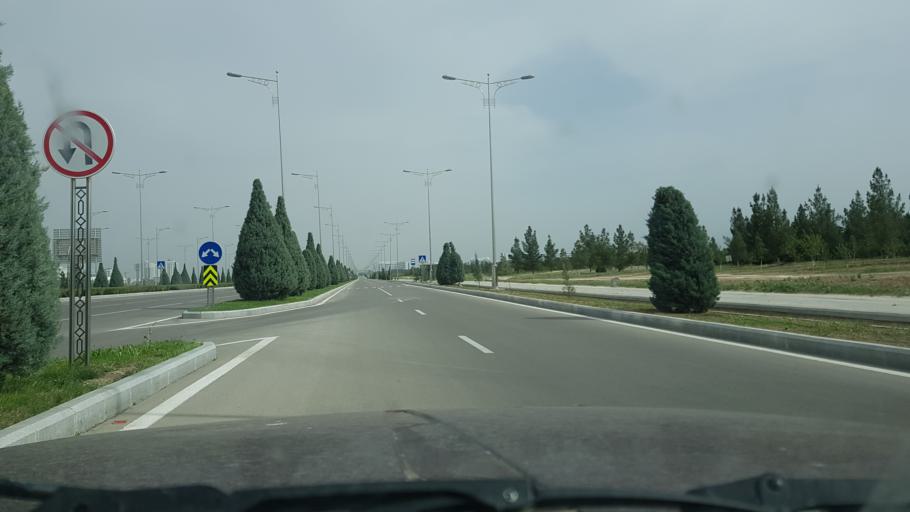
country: TM
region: Ahal
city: Ashgabat
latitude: 37.8873
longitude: 58.3378
